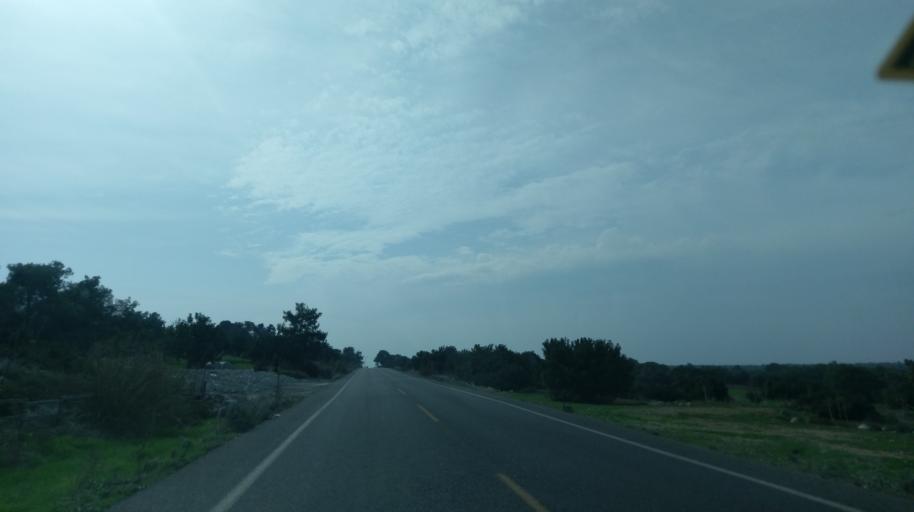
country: CY
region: Lefkosia
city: Morfou
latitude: 35.3084
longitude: 33.0481
